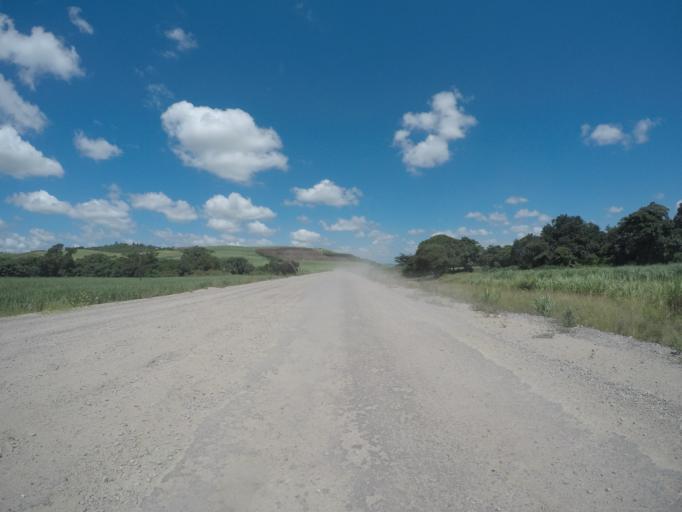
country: ZA
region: KwaZulu-Natal
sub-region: uThungulu District Municipality
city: Empangeni
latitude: -28.6452
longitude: 31.7667
